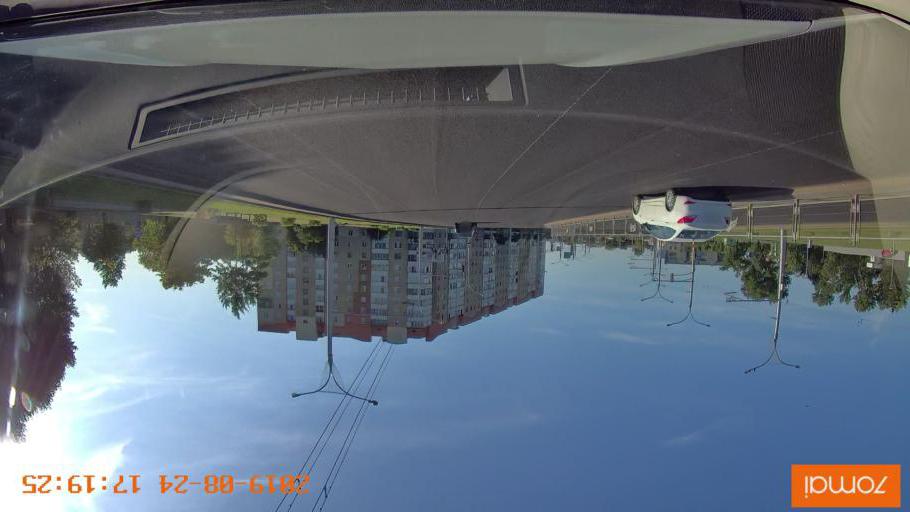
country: BY
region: Minsk
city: Vyaliki Trastsyanets
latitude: 53.8618
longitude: 27.6411
